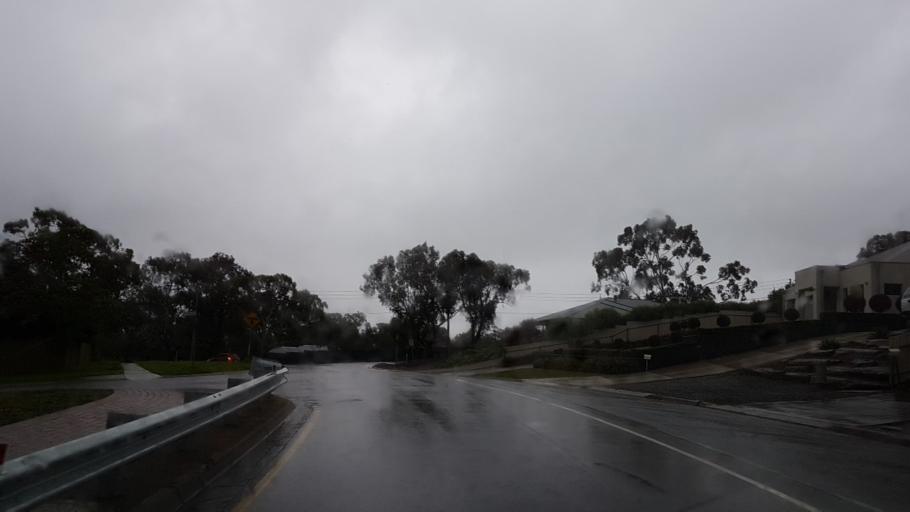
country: AU
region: South Australia
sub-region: Onkaparinga
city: Craigburn Farm
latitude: -35.0882
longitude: 138.5887
